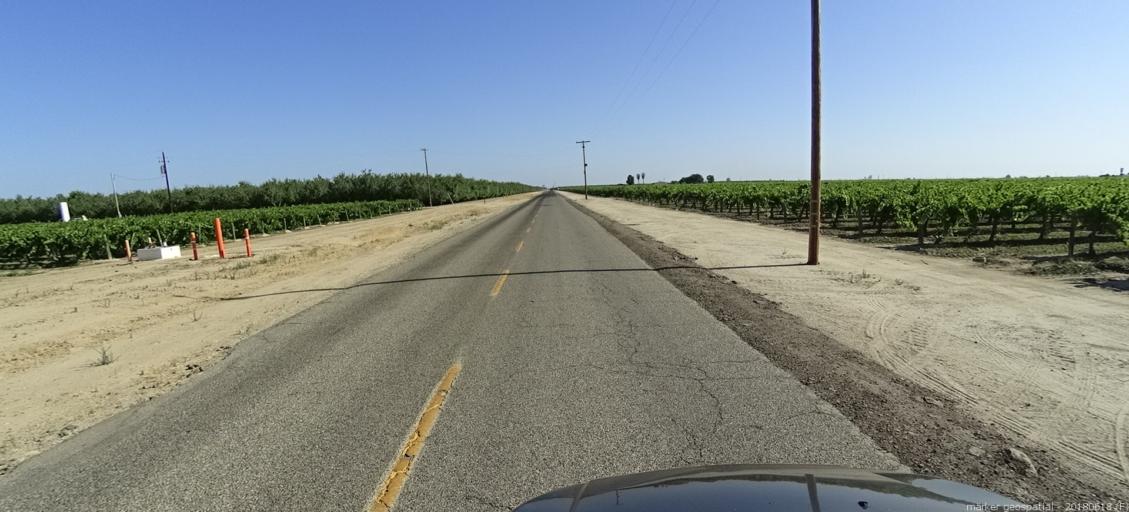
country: US
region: California
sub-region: Madera County
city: Parkwood
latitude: 36.8956
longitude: -120.1286
